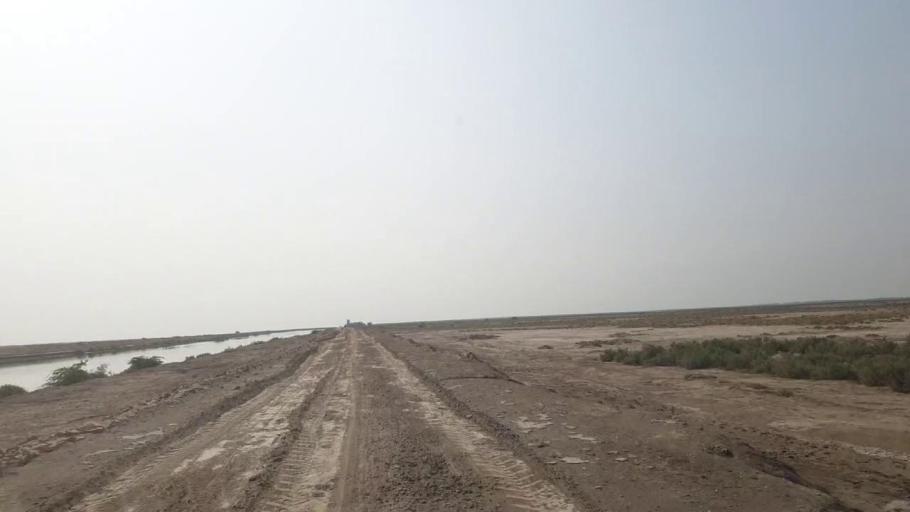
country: PK
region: Sindh
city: Kadhan
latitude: 24.3293
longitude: 68.8321
